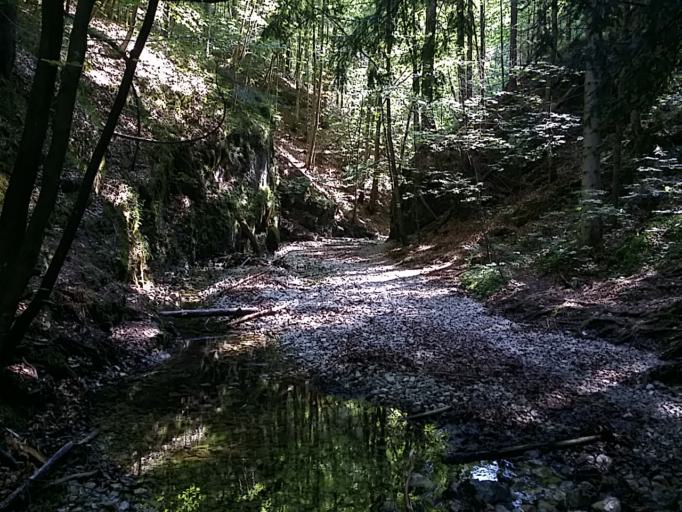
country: SK
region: Kosicky
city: Dobsina
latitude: 48.9374
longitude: 20.3569
